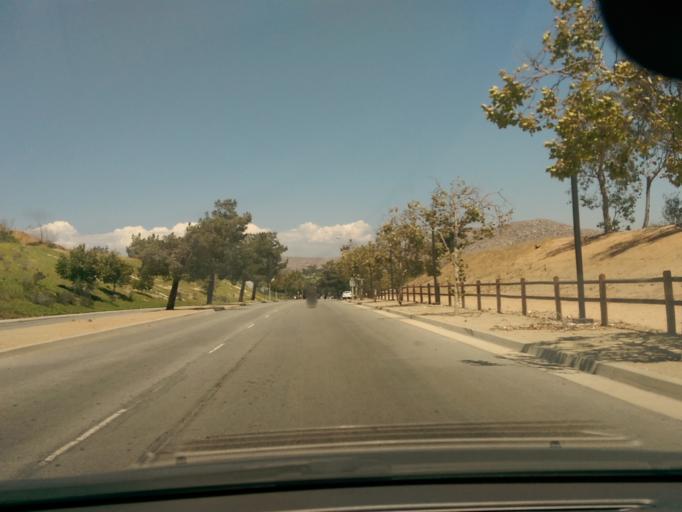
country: US
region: California
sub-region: Riverside County
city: Norco
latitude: 33.9164
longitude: -117.5644
